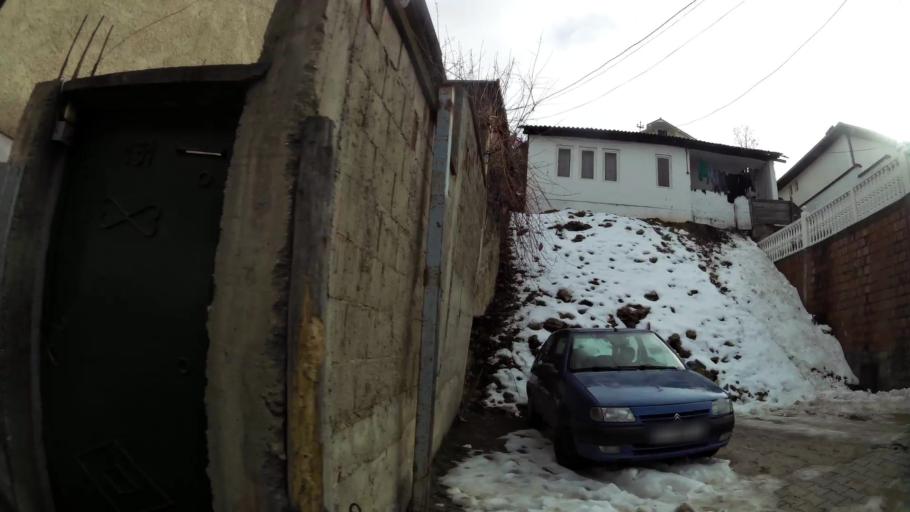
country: XK
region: Pristina
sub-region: Komuna e Prishtines
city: Pristina
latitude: 42.6772
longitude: 21.1760
